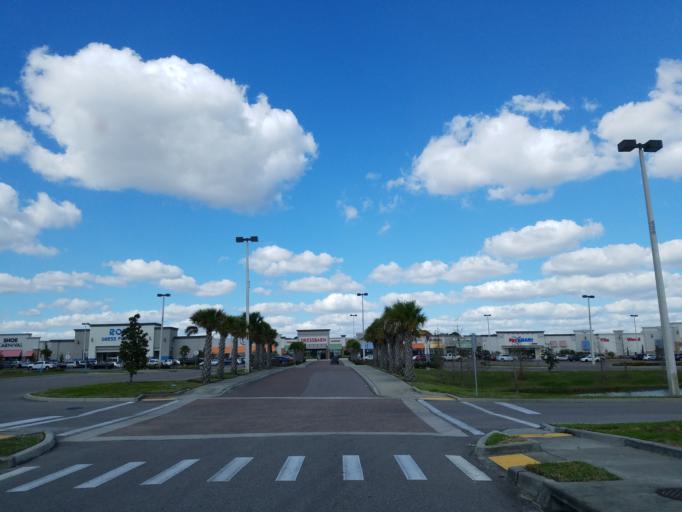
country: US
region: Florida
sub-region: Polk County
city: Gibsonia
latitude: 28.0887
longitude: -81.9686
